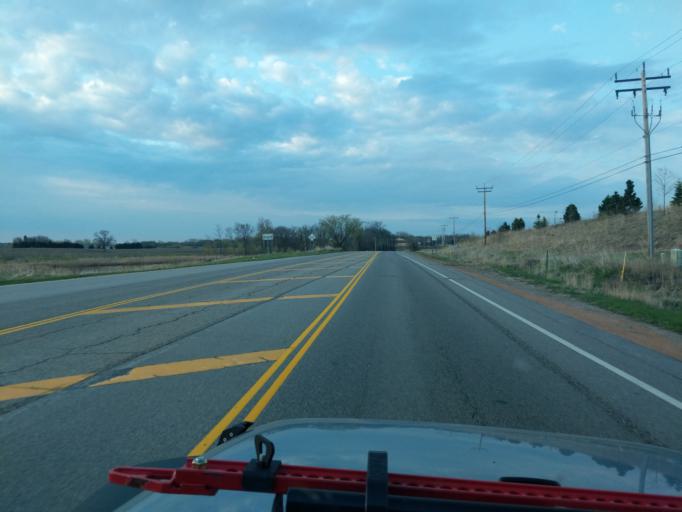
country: US
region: Minnesota
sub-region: Hennepin County
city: Rogers
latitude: 45.1816
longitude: -93.5232
